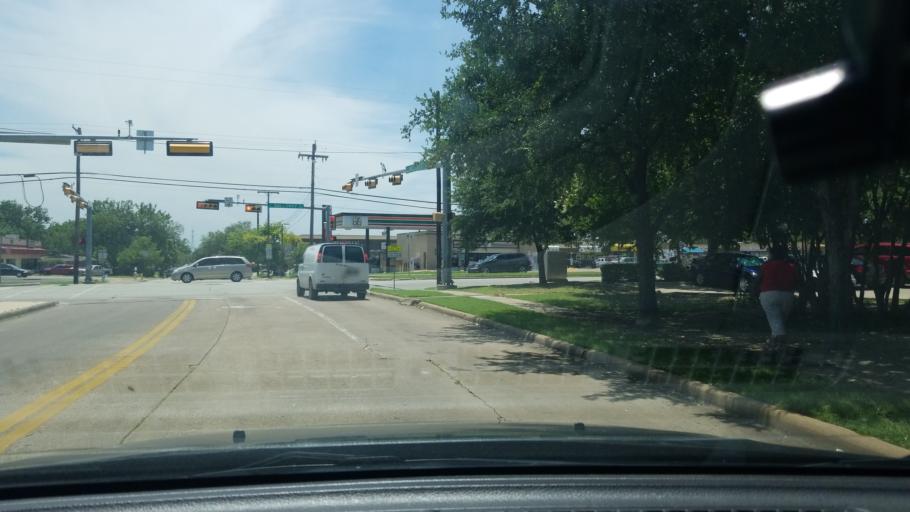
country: US
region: Texas
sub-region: Dallas County
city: Mesquite
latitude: 32.7871
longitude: -96.6056
